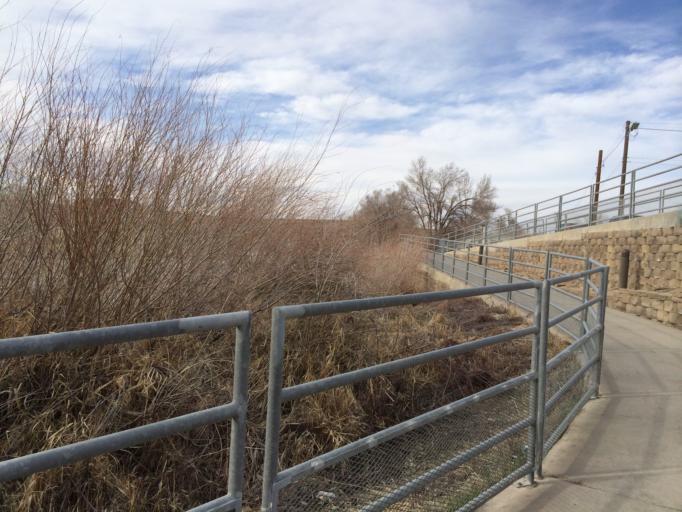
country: US
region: Wyoming
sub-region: Natrona County
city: Casper
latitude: 42.8573
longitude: -106.3271
